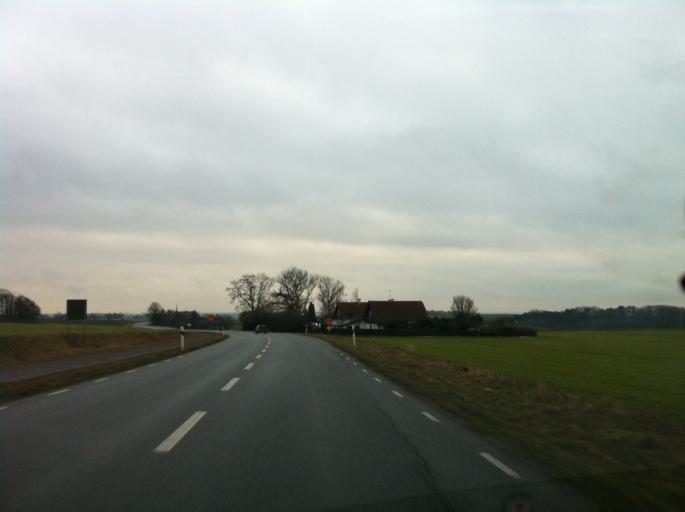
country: SE
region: Skane
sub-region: Helsingborg
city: Glumslov
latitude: 55.9394
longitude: 12.8144
